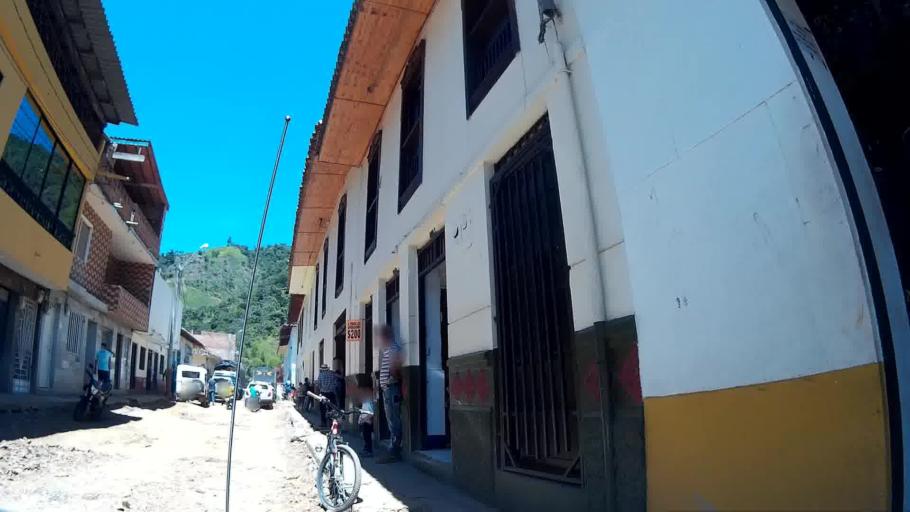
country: CO
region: Antioquia
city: Salgar
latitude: 5.9618
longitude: -75.9774
